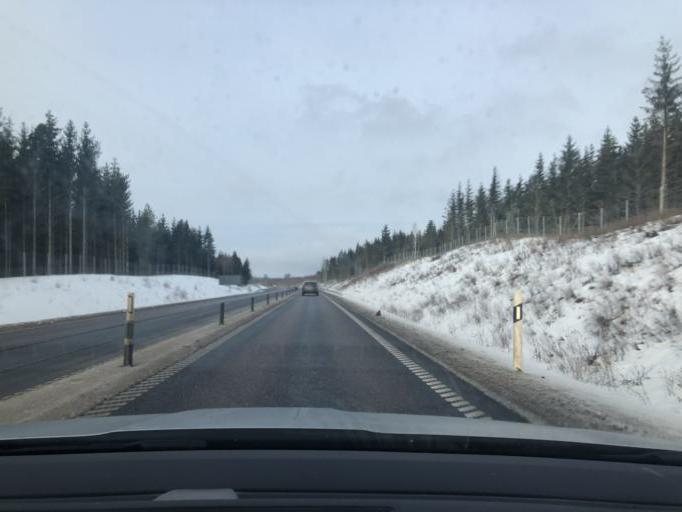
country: SE
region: OEstergoetland
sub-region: Motala Kommun
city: Borensberg
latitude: 58.5868
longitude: 15.1933
